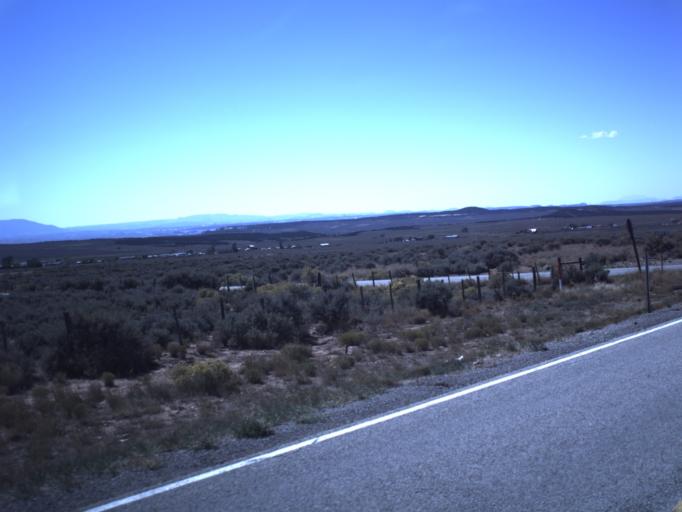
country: US
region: Utah
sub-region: Grand County
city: Moab
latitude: 38.3097
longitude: -109.2713
